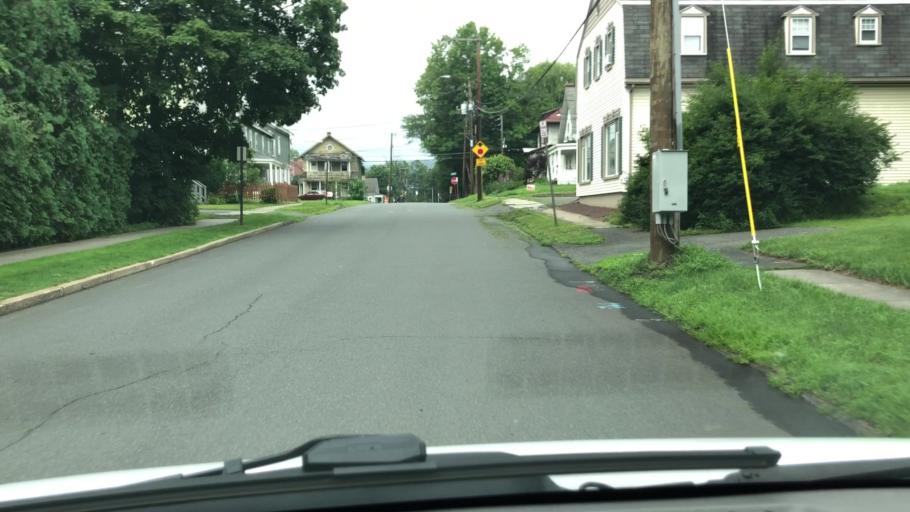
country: US
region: Massachusetts
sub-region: Franklin County
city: Greenfield
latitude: 42.5903
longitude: -72.6054
